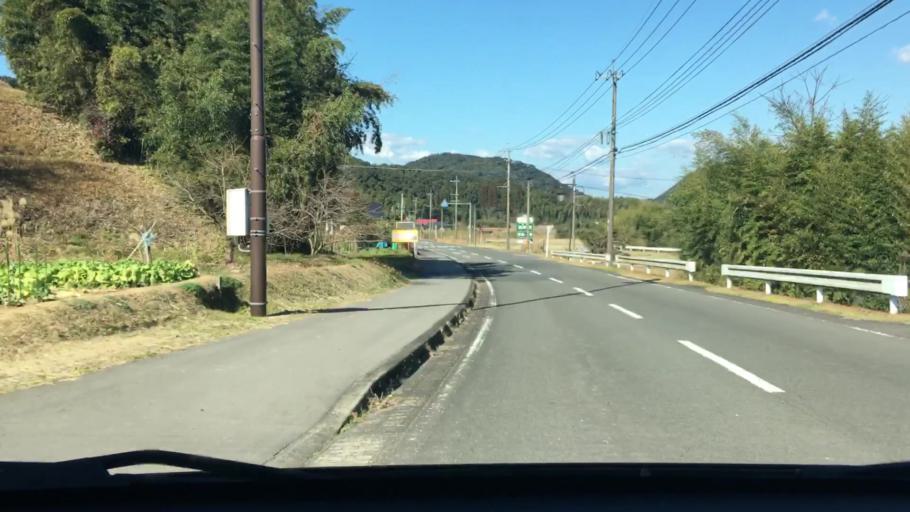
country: JP
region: Kagoshima
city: Satsumasendai
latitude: 31.7739
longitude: 130.4013
